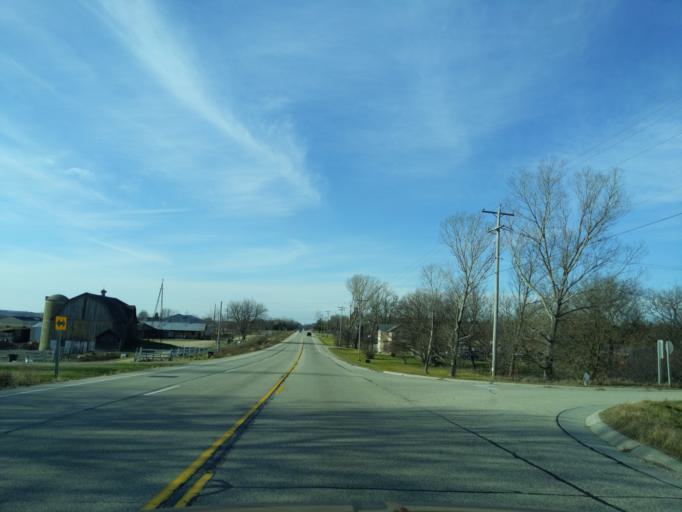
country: US
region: Wisconsin
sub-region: Walworth County
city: Whitewater
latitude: 42.8051
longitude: -88.6554
